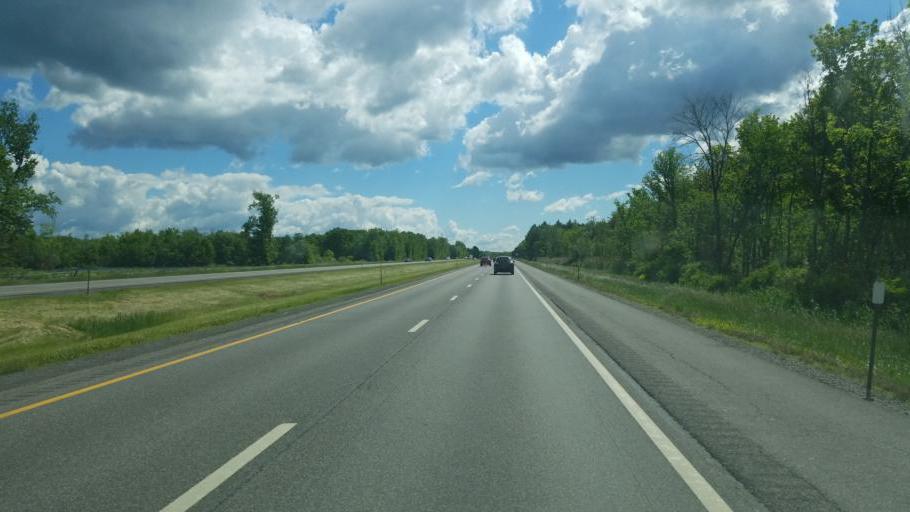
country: US
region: New York
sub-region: Madison County
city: Bolivar
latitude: 43.0920
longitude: -75.8994
